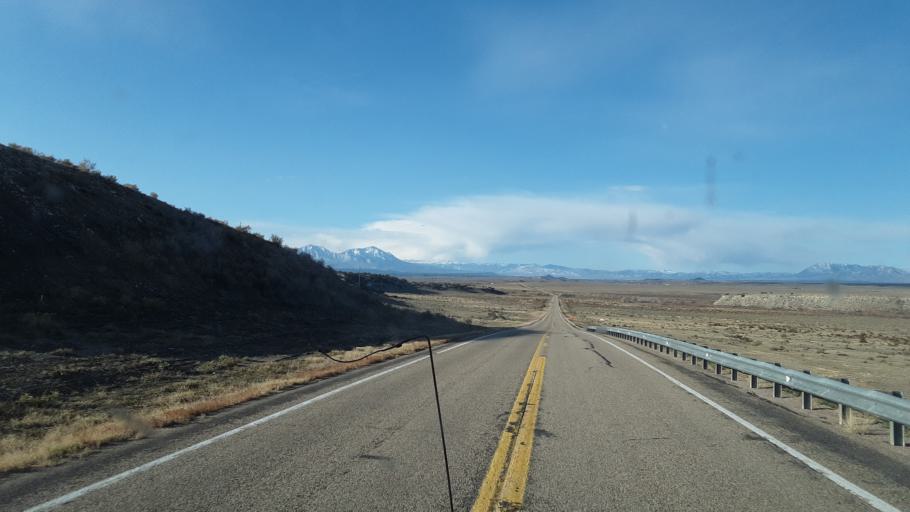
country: US
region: Colorado
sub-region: Huerfano County
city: Walsenburg
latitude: 37.6909
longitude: -104.6339
